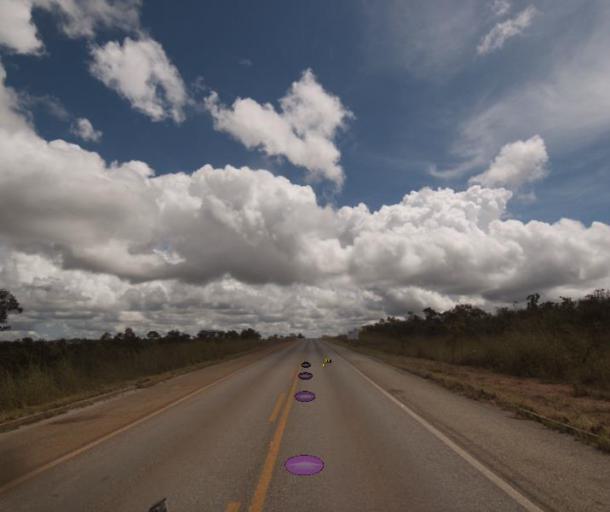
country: BR
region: Goias
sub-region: Pirenopolis
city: Pirenopolis
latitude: -15.7507
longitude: -48.6446
